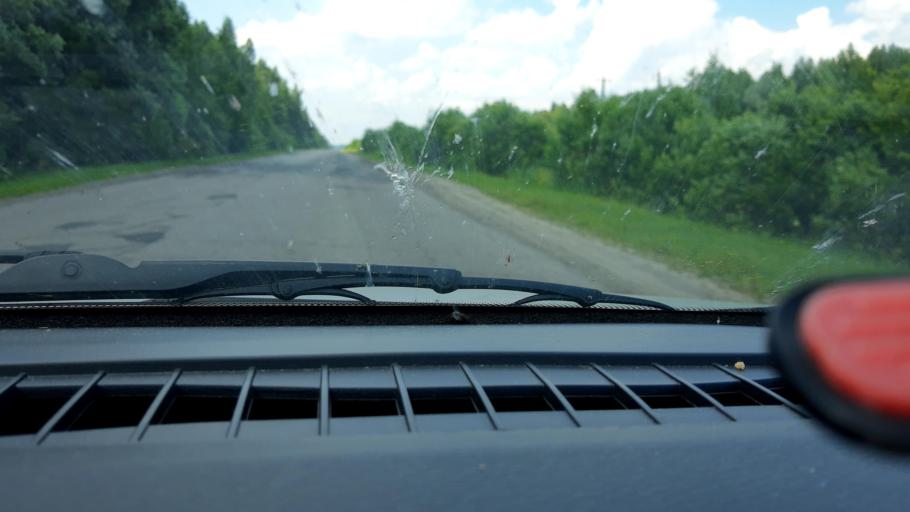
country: RU
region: Nizjnij Novgorod
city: Prudy
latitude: 57.4213
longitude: 46.0671
